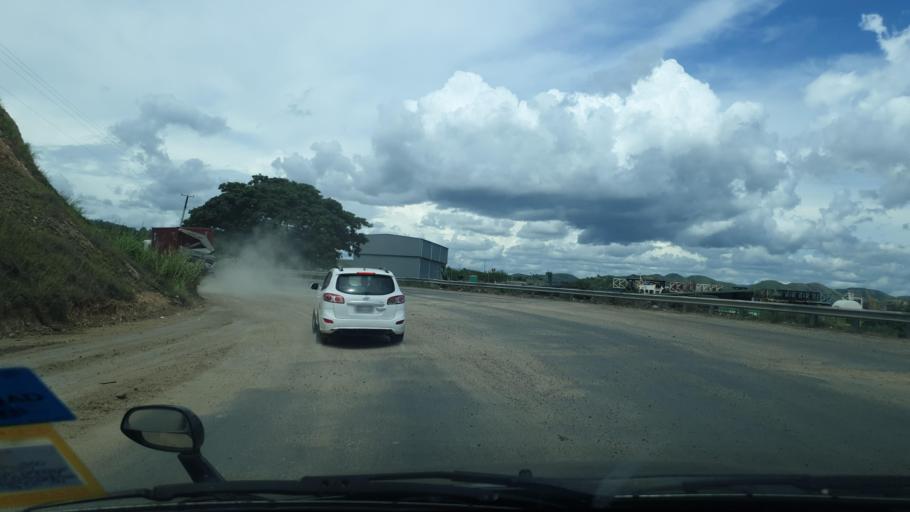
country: PG
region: National Capital
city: Port Moresby
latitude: -9.4201
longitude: 147.0988
